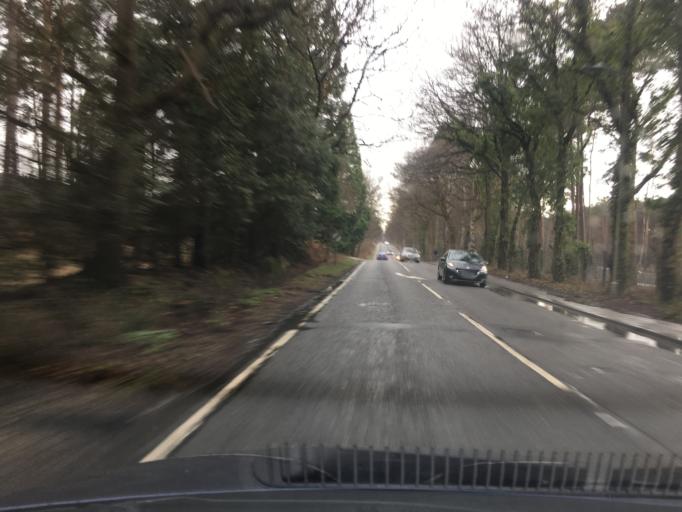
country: GB
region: England
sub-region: Bracknell Forest
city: Crowthorne
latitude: 51.3775
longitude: -0.7816
